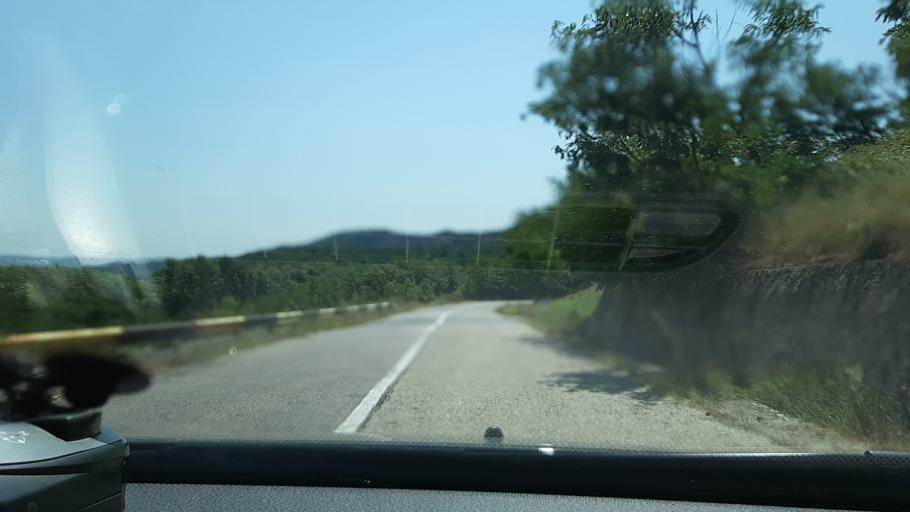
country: RO
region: Gorj
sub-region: Comuna Bustuchin
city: Bustuchin
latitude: 44.9142
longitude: 23.7689
